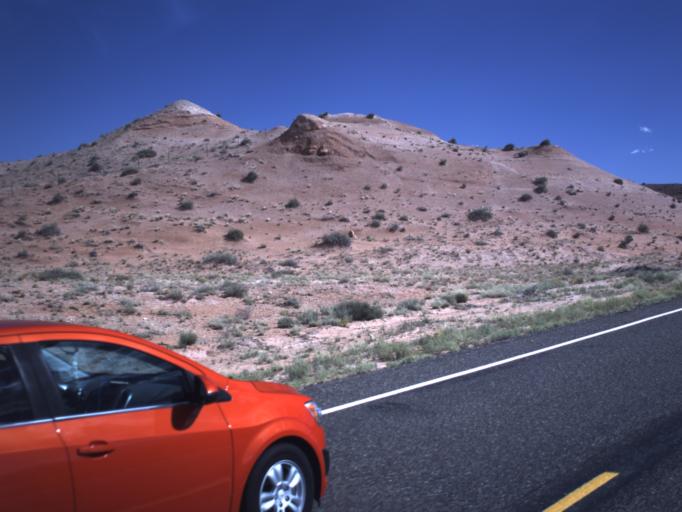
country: US
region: Utah
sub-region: Emery County
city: Ferron
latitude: 38.3071
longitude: -110.6711
